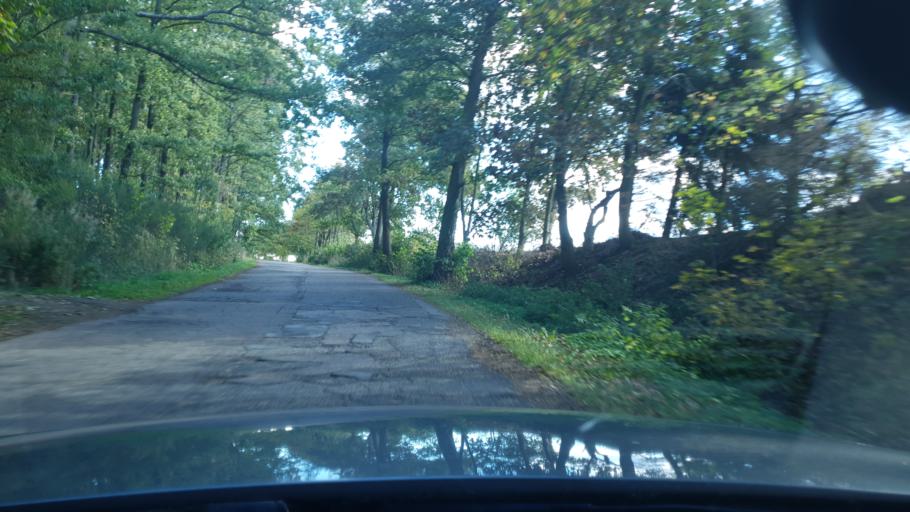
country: PL
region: Pomeranian Voivodeship
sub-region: Powiat pucki
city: Zelistrzewo
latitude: 54.6887
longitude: 18.4272
